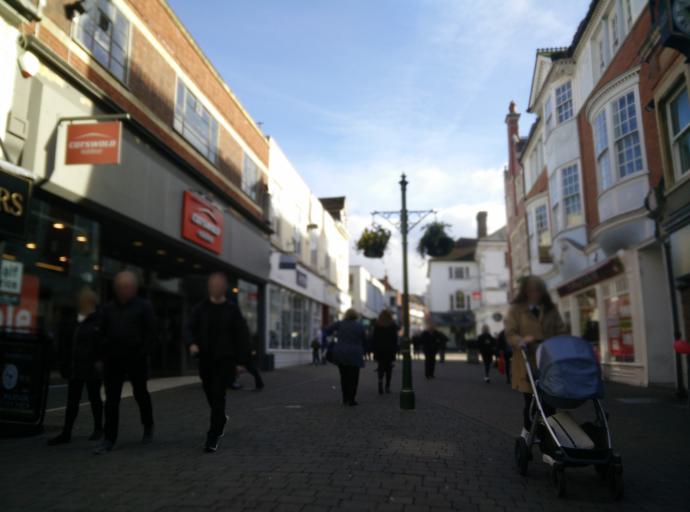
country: GB
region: England
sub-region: West Sussex
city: Horsham
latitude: 51.0625
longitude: -0.3296
